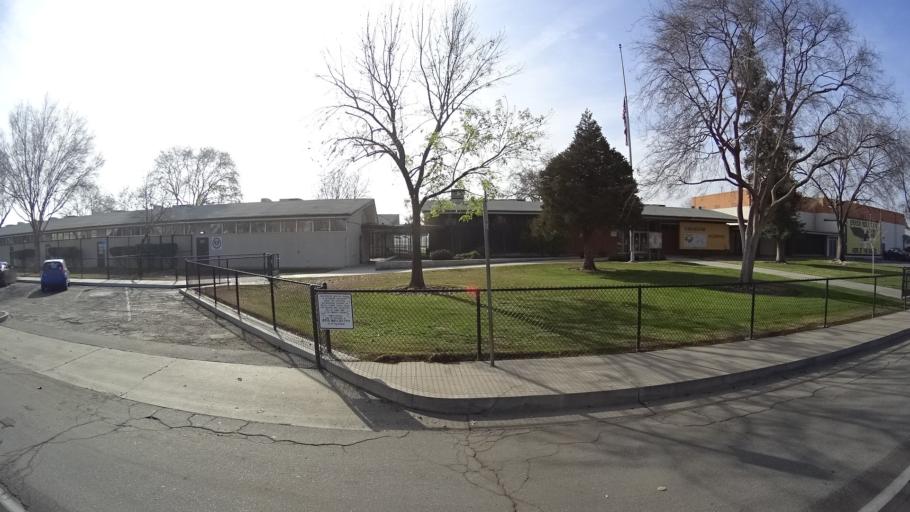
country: US
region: California
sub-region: Kern County
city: Bakersfield
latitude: 35.3612
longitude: -119.0111
